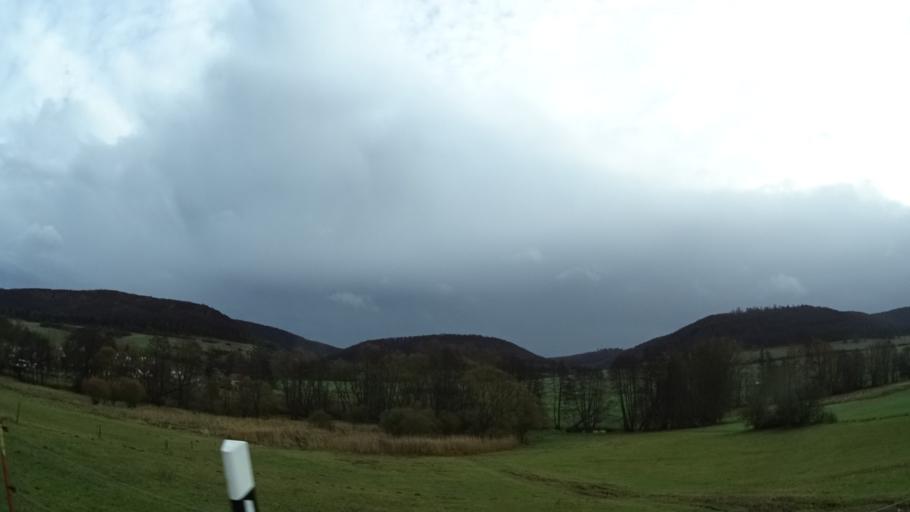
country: DE
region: Thuringia
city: Rippershausen
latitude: 50.5743
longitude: 10.3268
